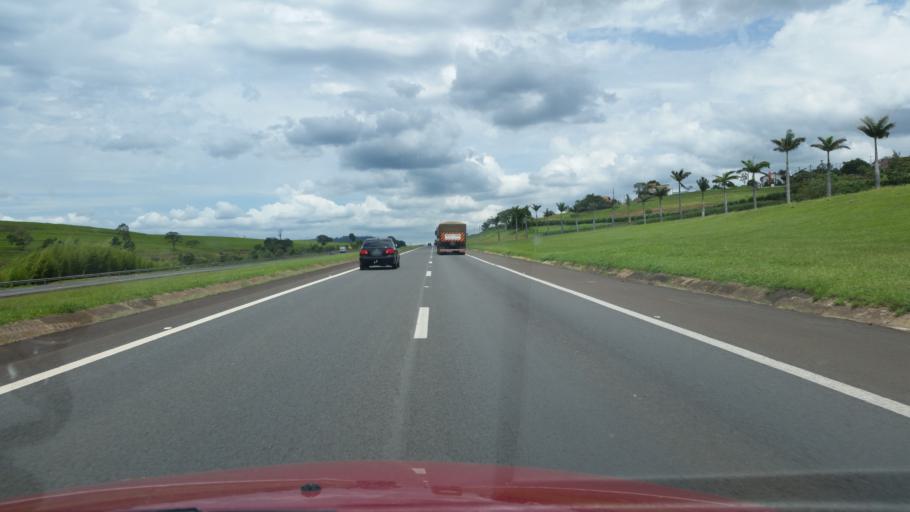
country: BR
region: Sao Paulo
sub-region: Itatinga
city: Itatinga
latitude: -23.1418
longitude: -48.4254
